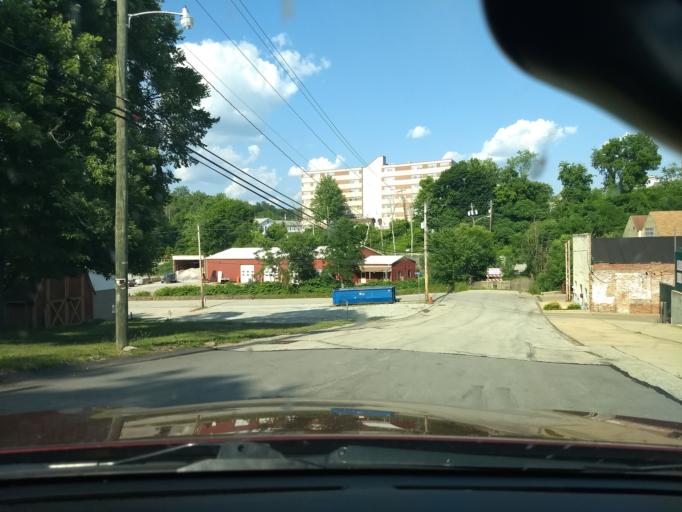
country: US
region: Pennsylvania
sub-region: Westmoreland County
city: Irwin
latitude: 40.3336
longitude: -79.7133
